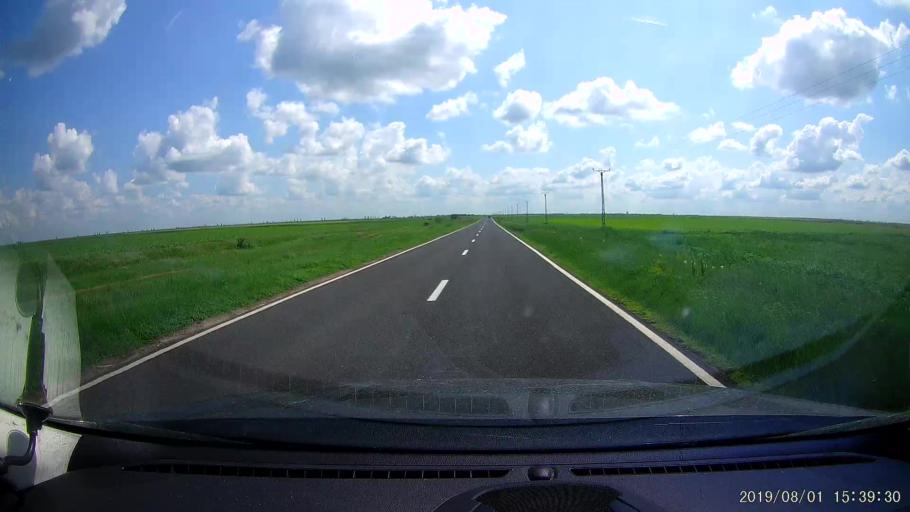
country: RO
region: Braila
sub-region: Comuna Baraganul
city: Baraganul
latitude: 44.8562
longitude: 27.5585
